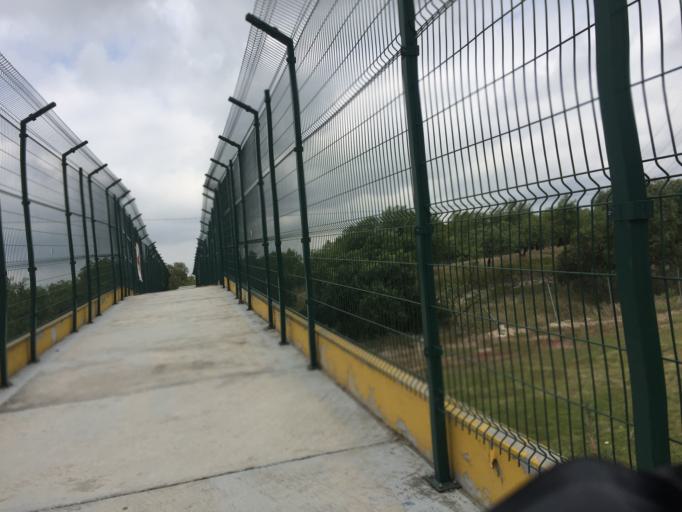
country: MX
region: Mexico
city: Cuautitlan Izcalli
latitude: 19.6561
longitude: -99.1995
